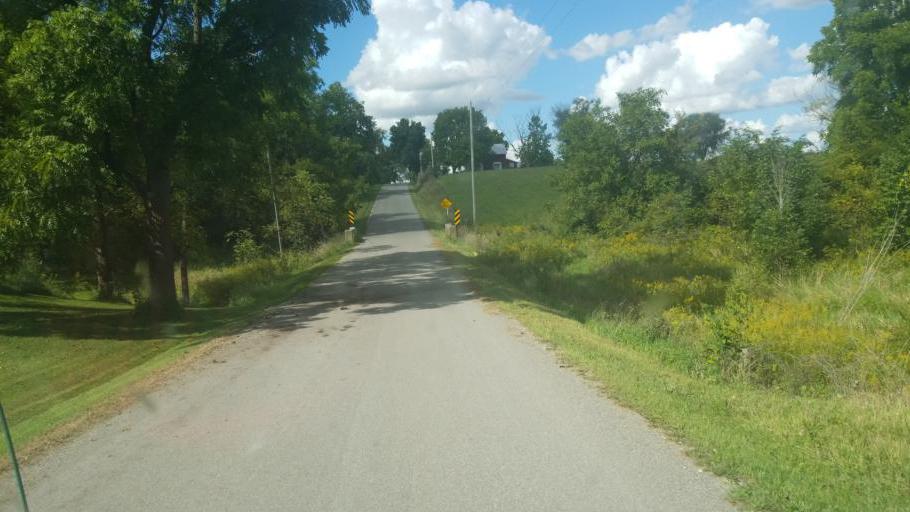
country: US
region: Ohio
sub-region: Hardin County
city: Kenton
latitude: 40.5421
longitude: -83.5437
